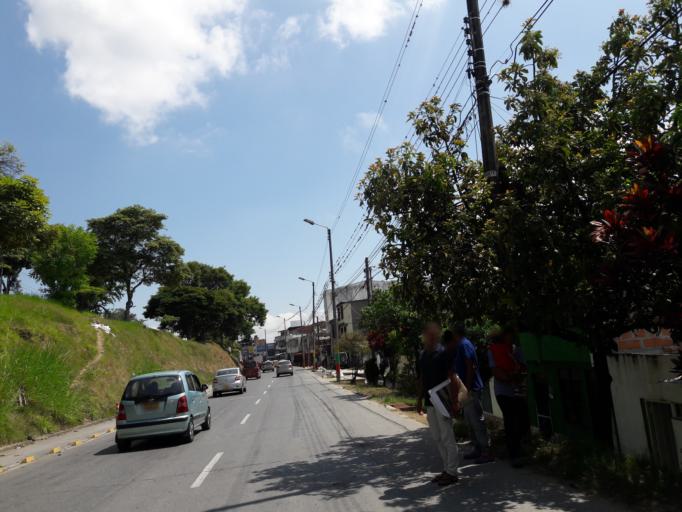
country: CO
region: Tolima
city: Ibague
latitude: 4.4357
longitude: -75.2208
